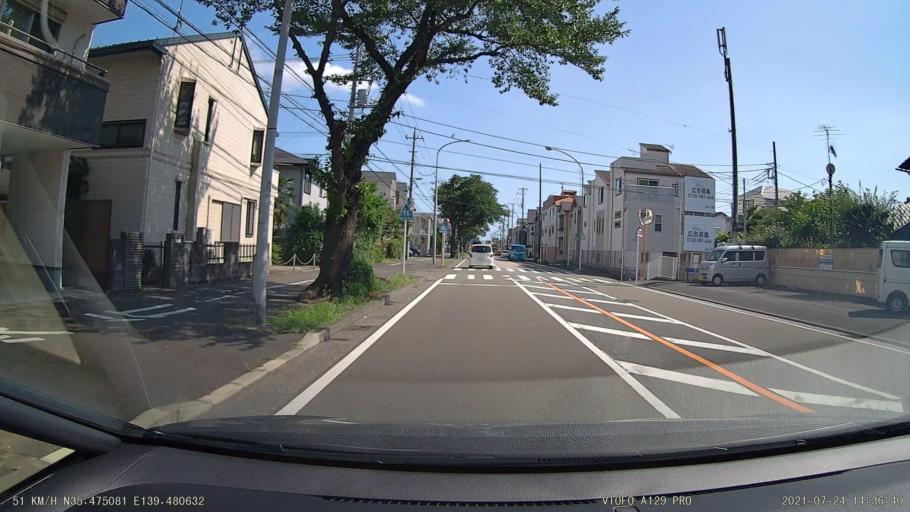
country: JP
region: Kanagawa
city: Minami-rinkan
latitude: 35.4751
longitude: 139.4806
